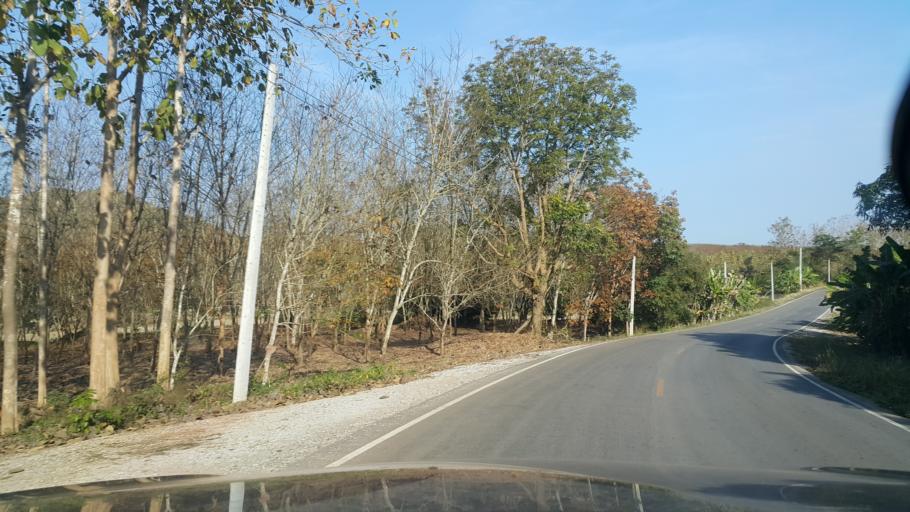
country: TH
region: Loei
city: Chiang Khan
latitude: 17.8238
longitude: 101.6262
